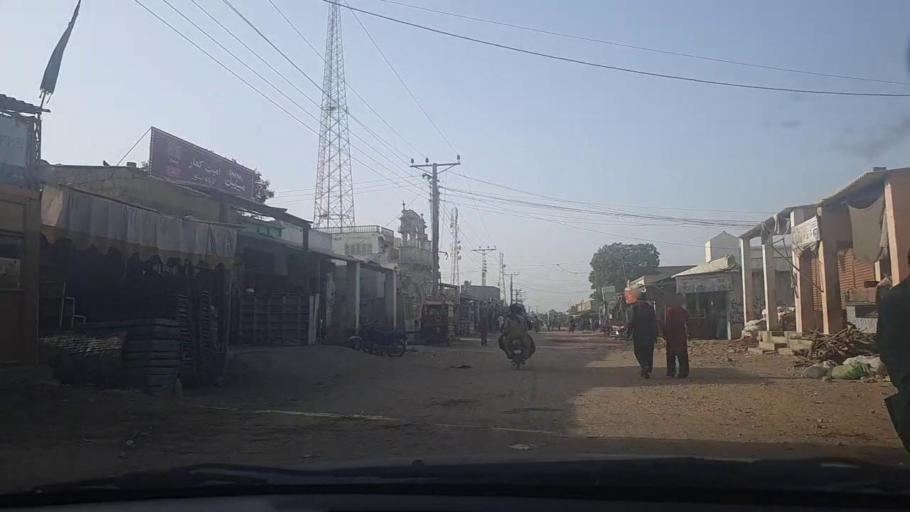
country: PK
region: Sindh
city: Keti Bandar
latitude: 24.3017
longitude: 67.6060
